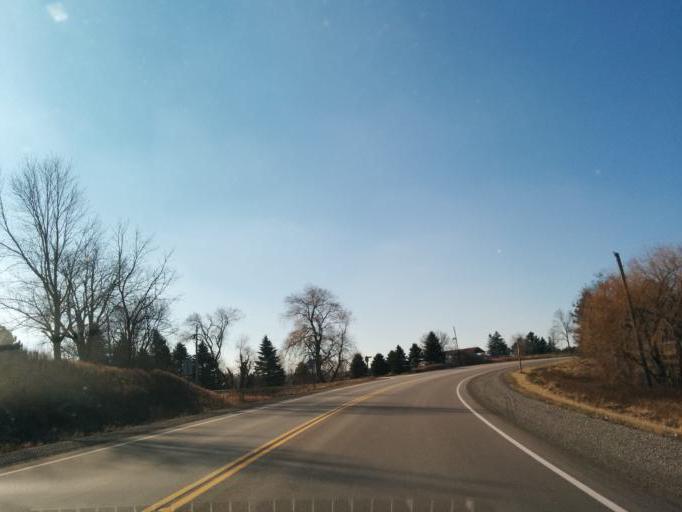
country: CA
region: Ontario
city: Brantford
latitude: 43.0411
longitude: -80.2732
